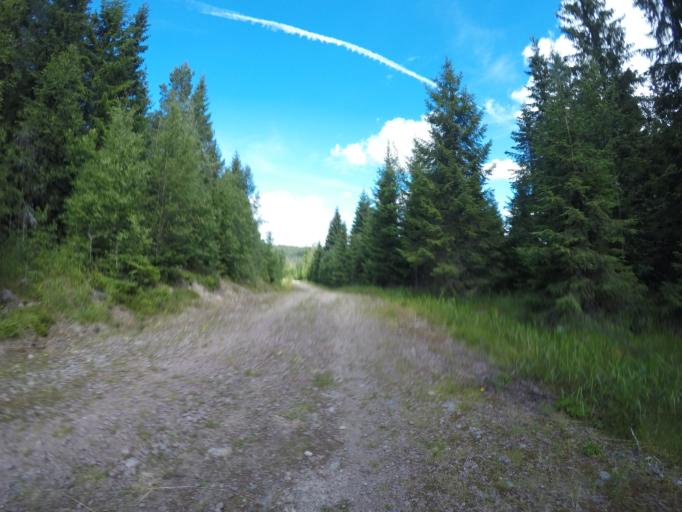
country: SE
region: Vaermland
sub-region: Filipstads Kommun
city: Lesjofors
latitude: 60.0772
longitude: 14.4591
